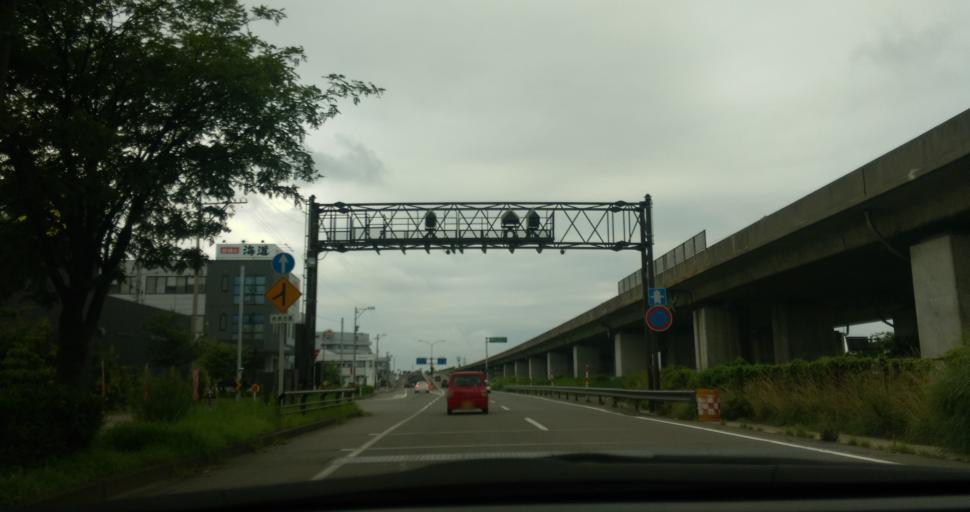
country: JP
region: Ishikawa
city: Kanazawa-shi
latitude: 36.5885
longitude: 136.6275
